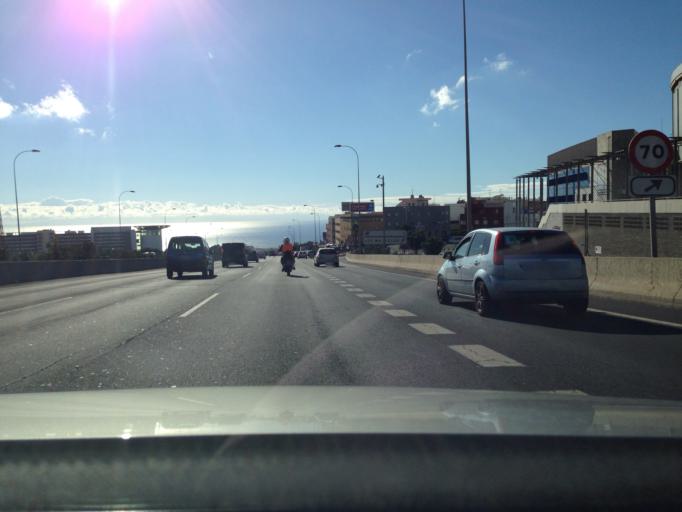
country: ES
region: Canary Islands
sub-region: Provincia de Santa Cruz de Tenerife
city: La Laguna
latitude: 28.4595
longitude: -16.2968
